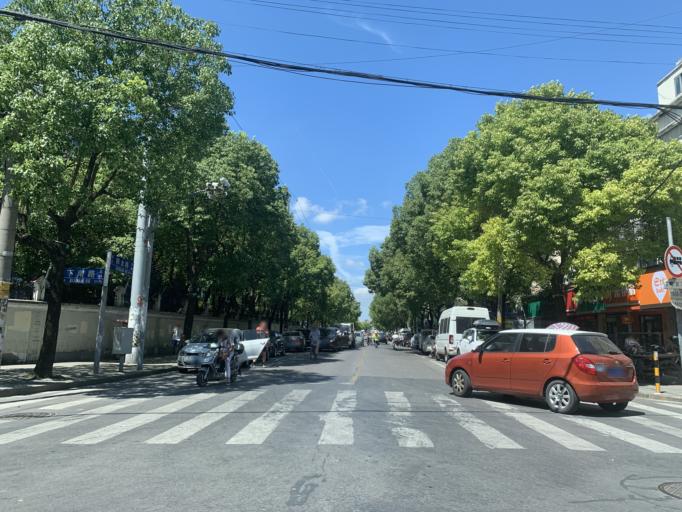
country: CN
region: Shanghai Shi
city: Huamu
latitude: 31.1738
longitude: 121.5360
